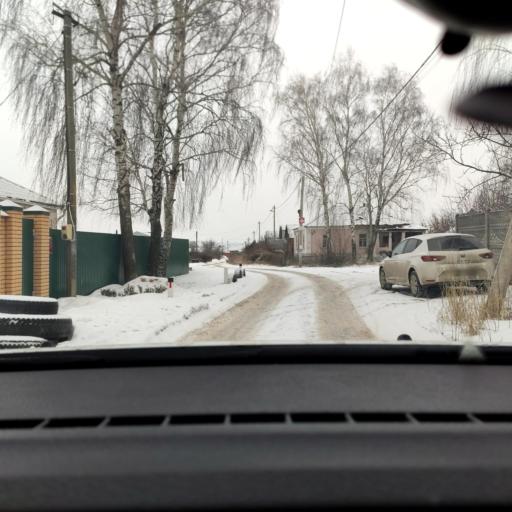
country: RU
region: Voronezj
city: Podgornoye
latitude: 51.7939
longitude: 39.1442
